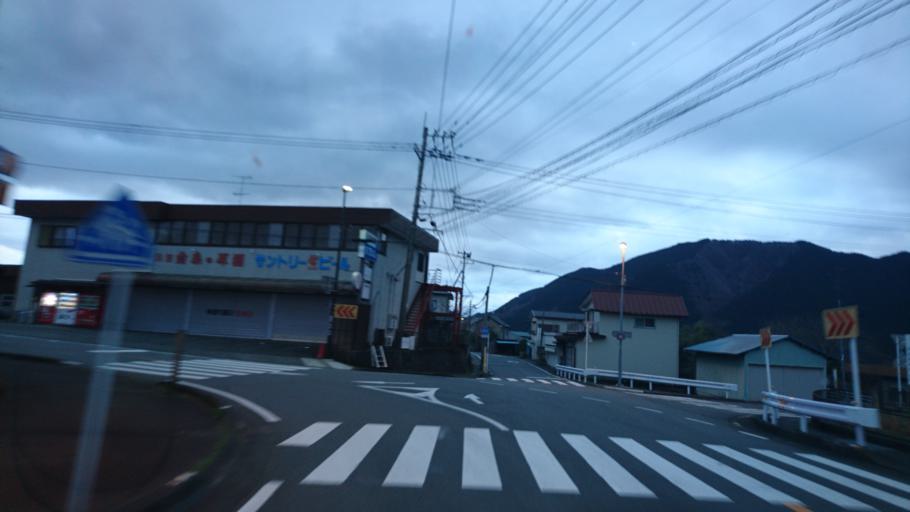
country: JP
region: Shizuoka
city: Fujinomiya
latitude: 35.3114
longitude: 138.5769
